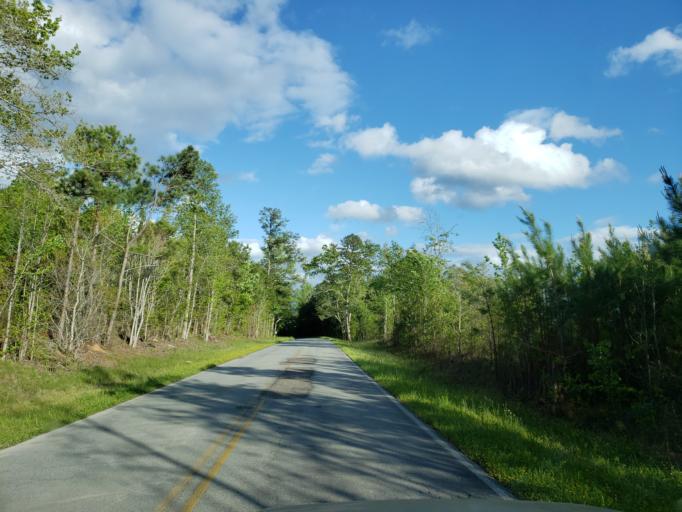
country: US
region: Georgia
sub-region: Haralson County
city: Tallapoosa
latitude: 33.7807
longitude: -85.3182
